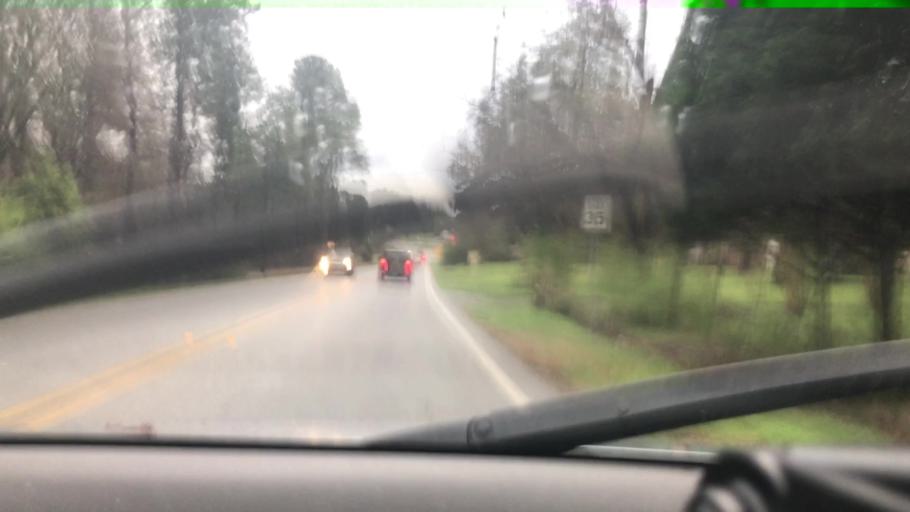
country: US
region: Georgia
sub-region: Oglethorpe County
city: Lexington
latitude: 33.8832
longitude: -83.1530
